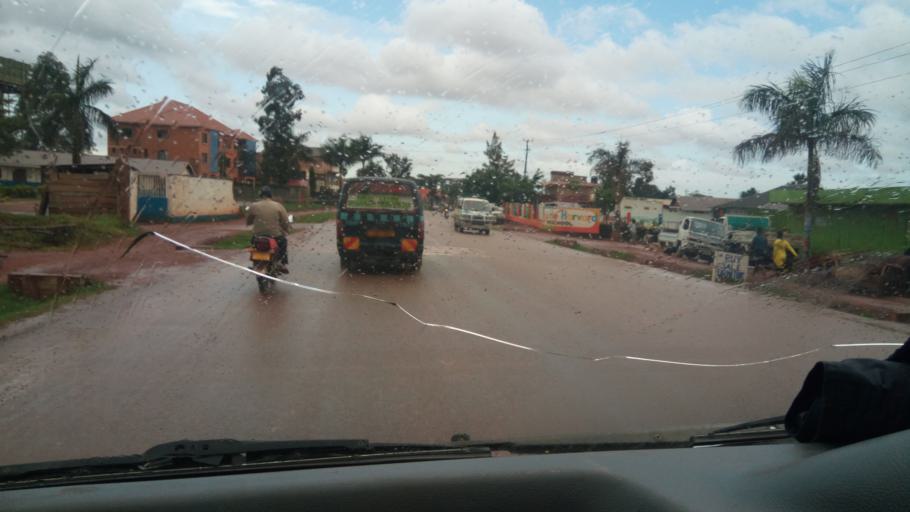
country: UG
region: Central Region
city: Kampala Central Division
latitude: 0.3646
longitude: 32.5277
